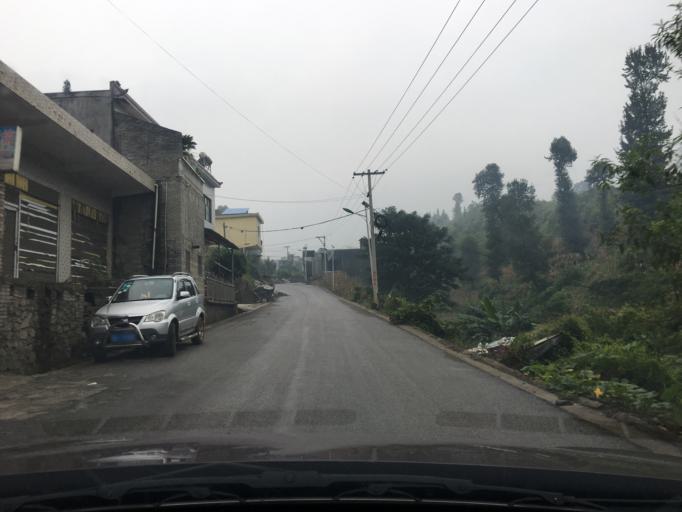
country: CN
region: Guizhou Sheng
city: Liupanshui
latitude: 26.0575
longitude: 105.1285
